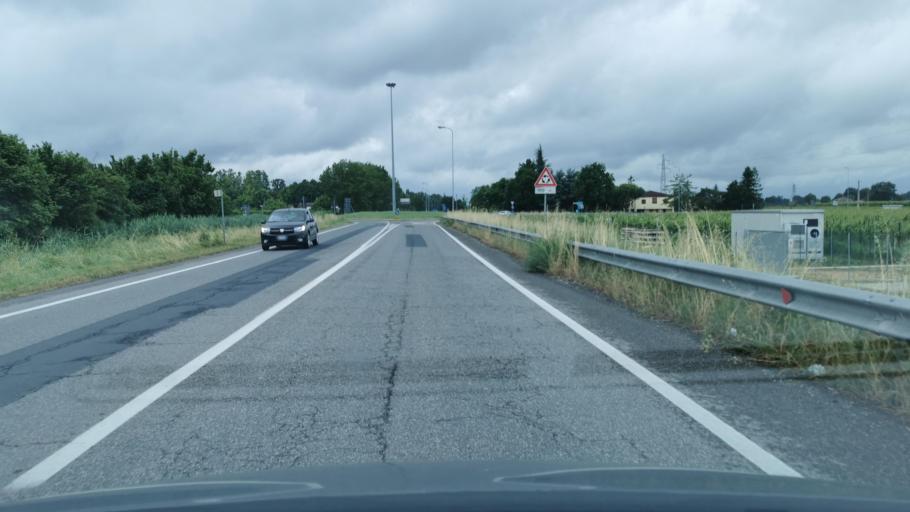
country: IT
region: Emilia-Romagna
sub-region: Provincia di Ravenna
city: Cotignola
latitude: 44.3845
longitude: 11.9526
